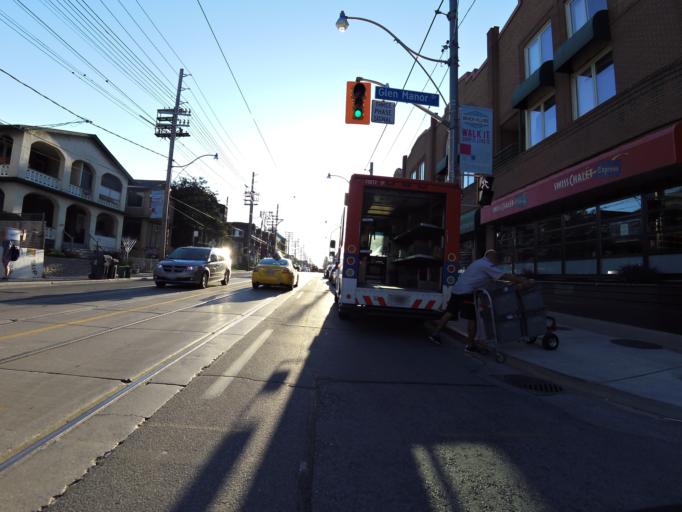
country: CA
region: Ontario
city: Scarborough
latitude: 43.6715
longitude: -79.2928
